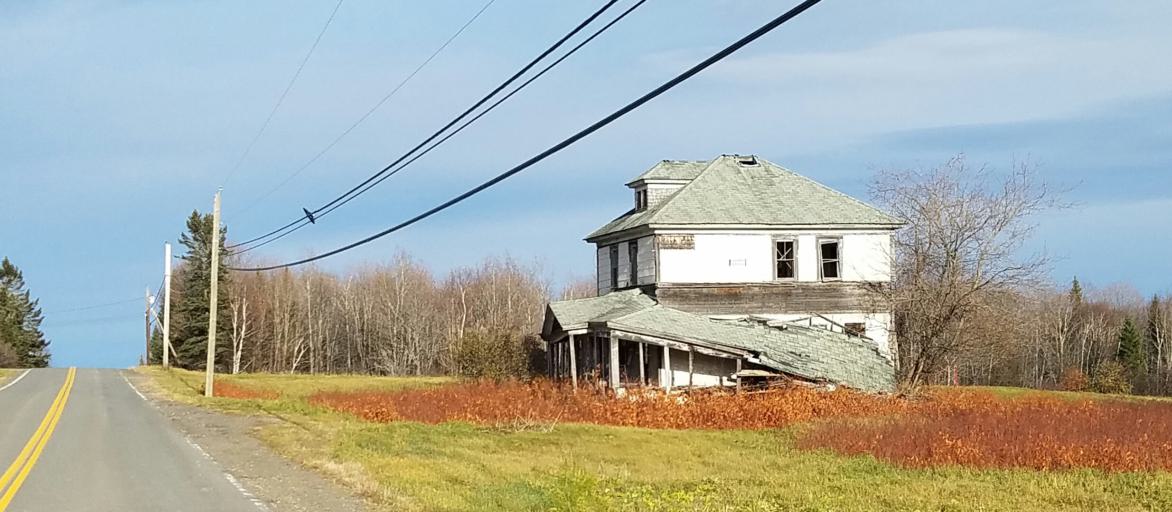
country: US
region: Maine
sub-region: Aroostook County
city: Presque Isle
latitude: 46.6400
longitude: -68.3752
